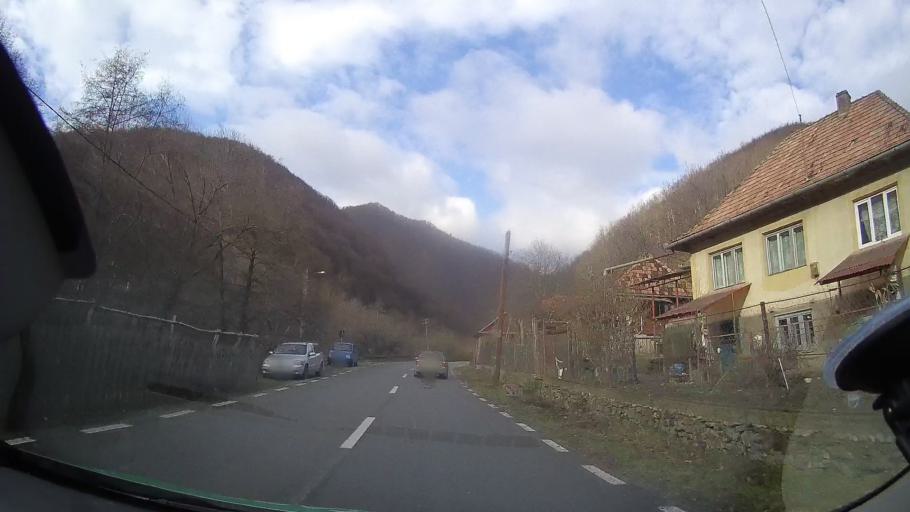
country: RO
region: Cluj
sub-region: Comuna Valea Ierii
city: Valea Ierii
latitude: 46.6176
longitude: 23.3980
